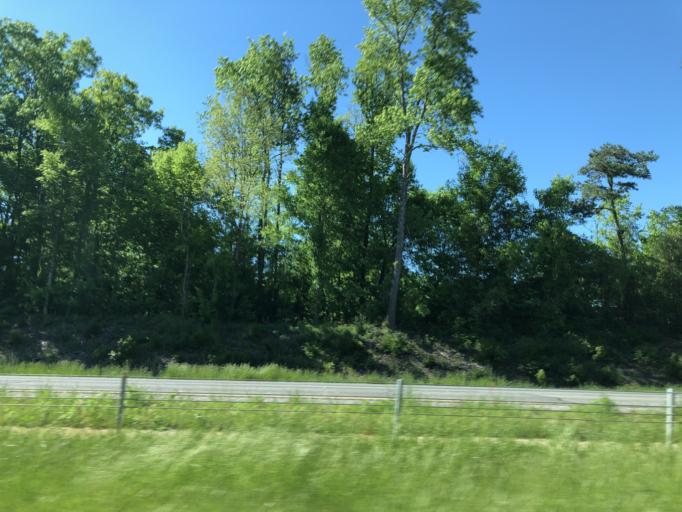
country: US
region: Georgia
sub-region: Clarke County
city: Country Club Estates
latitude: 33.9445
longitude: -83.4532
